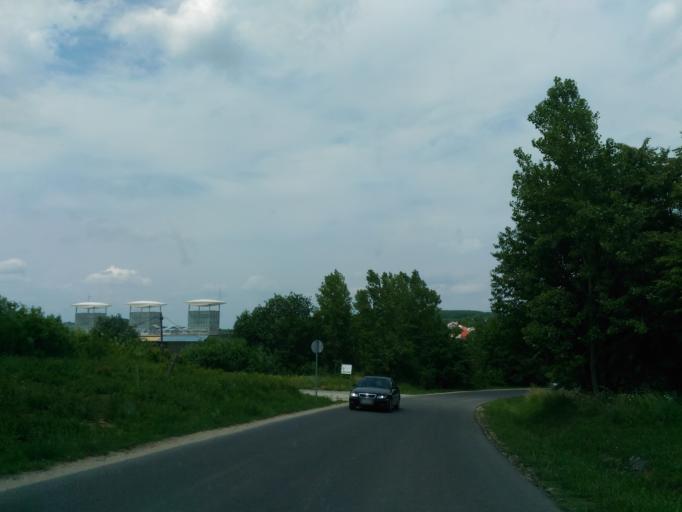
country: HU
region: Baranya
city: Komlo
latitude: 46.1849
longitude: 18.2387
